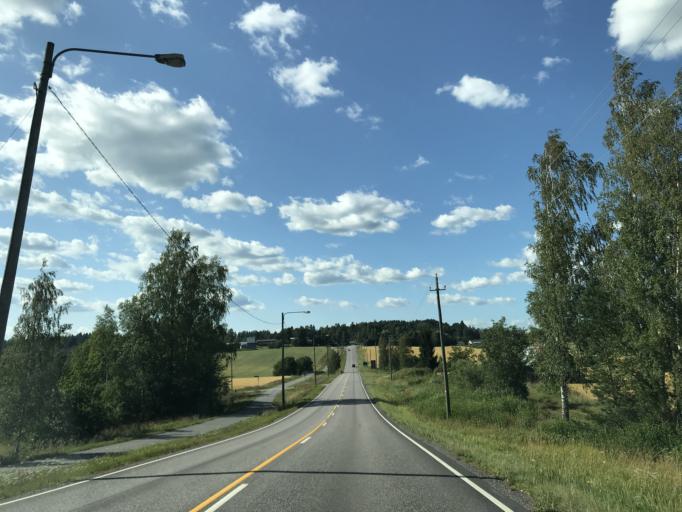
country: FI
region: Uusimaa
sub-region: Helsinki
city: Nurmijaervi
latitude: 60.4171
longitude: 24.8741
